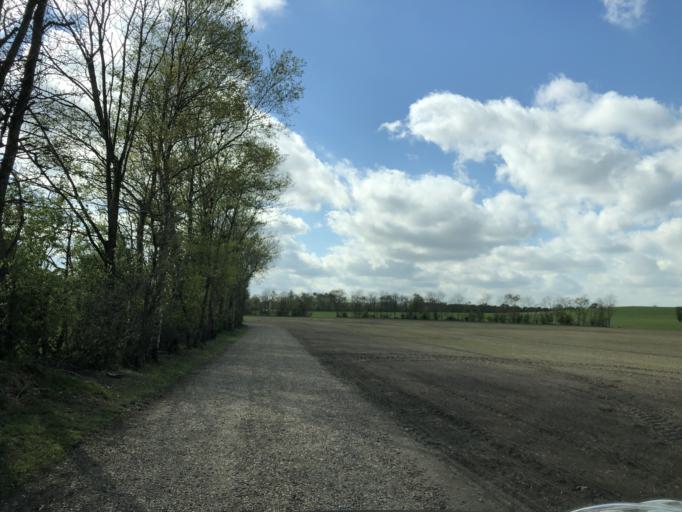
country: DK
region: Central Jutland
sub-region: Herning Kommune
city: Avlum
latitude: 56.2965
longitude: 8.7468
